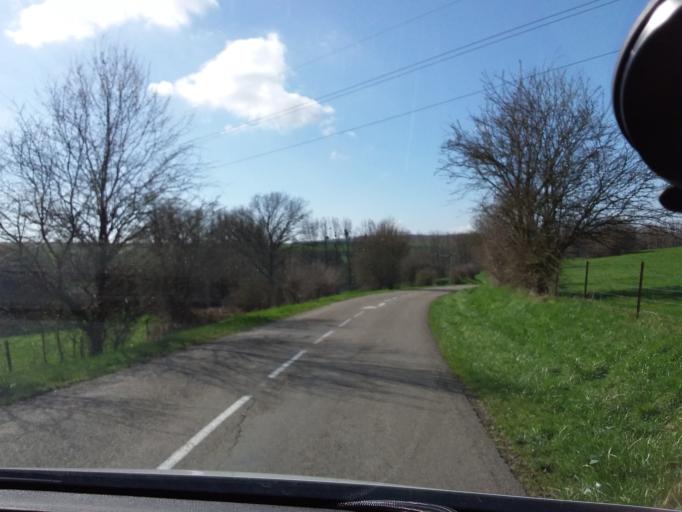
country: FR
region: Picardie
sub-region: Departement de l'Aisne
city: Origny-en-Thierache
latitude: 49.8001
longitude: 4.0091
